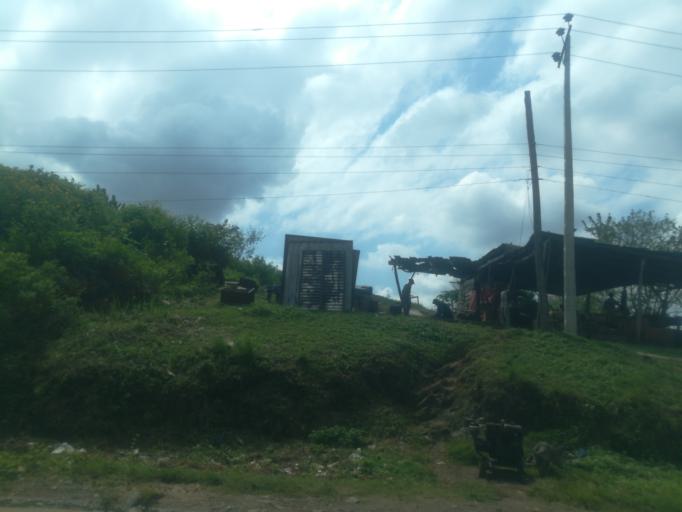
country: NG
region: Oyo
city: Egbeda
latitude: 7.4268
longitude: 3.9961
